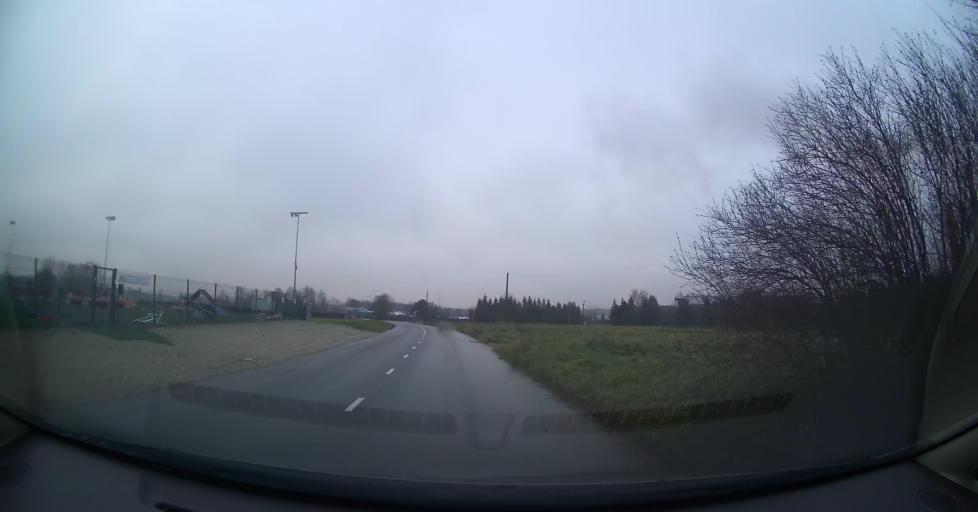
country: EE
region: Tartu
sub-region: Tartu linn
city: Tartu
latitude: 58.3718
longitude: 26.7940
